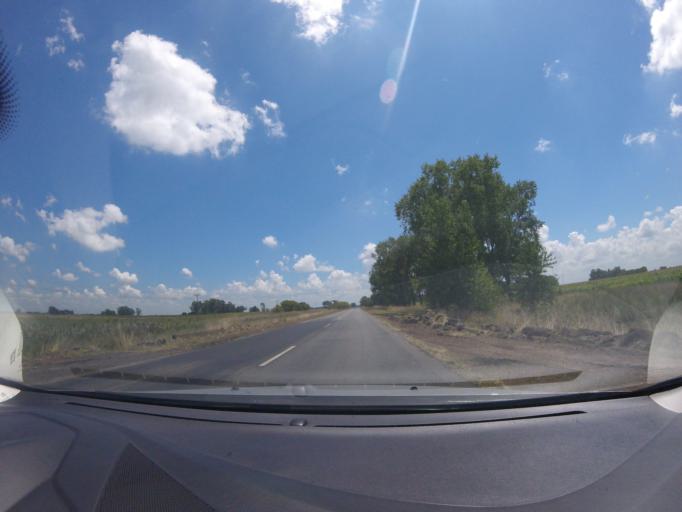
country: AR
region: Buenos Aires
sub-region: Partido de Las Flores
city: Las Flores
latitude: -36.1540
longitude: -59.0712
